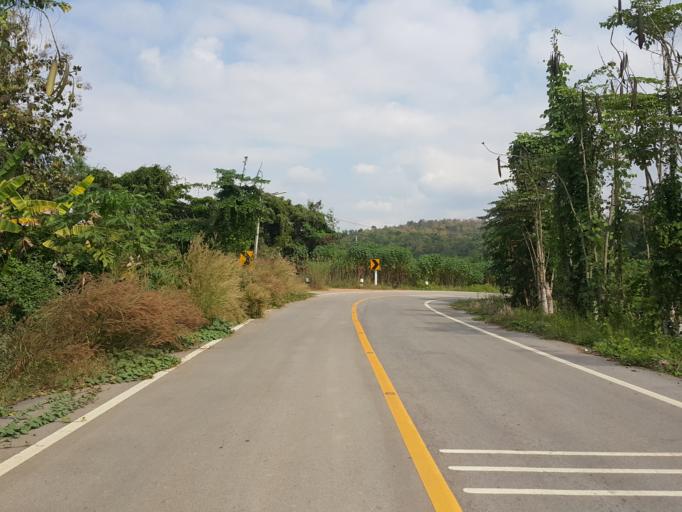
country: TH
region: Sukhothai
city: Thung Saliam
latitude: 17.4543
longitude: 99.5948
